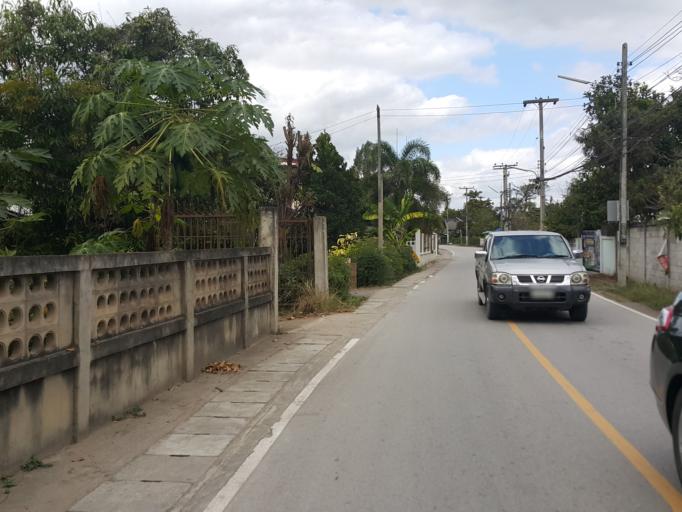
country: TH
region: Chiang Mai
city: San Sai
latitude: 18.8650
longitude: 99.1382
